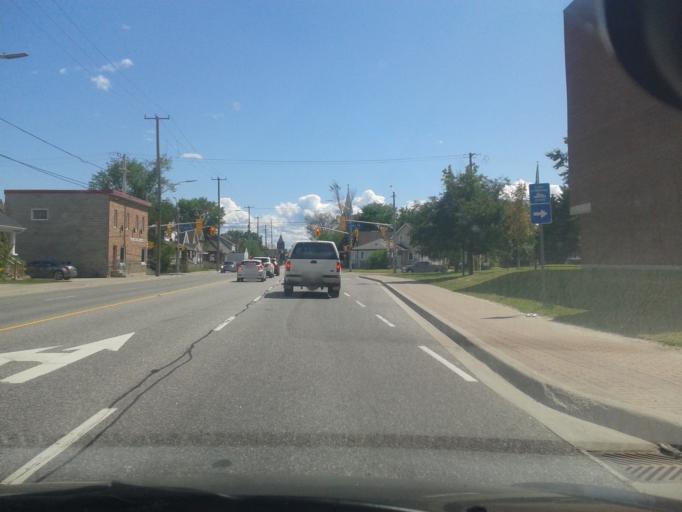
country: CA
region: Ontario
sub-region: Nipissing District
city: North Bay
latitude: 46.3187
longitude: -79.4662
